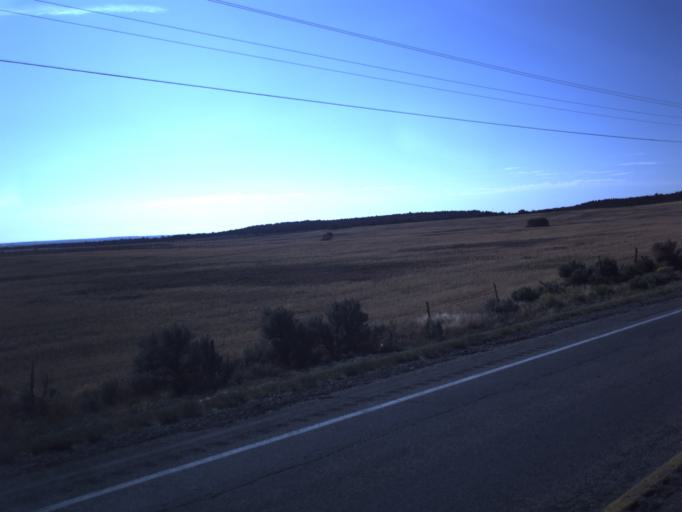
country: US
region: Utah
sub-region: San Juan County
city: Monticello
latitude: 37.9279
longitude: -109.3461
